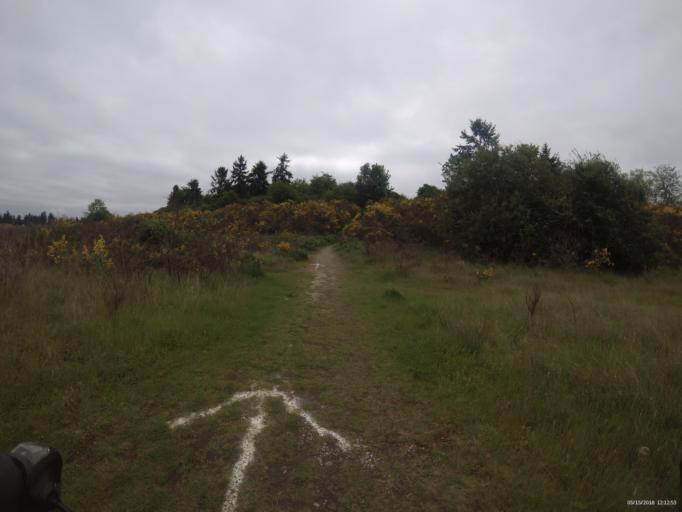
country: US
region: Washington
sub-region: Pierce County
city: Steilacoom
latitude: 47.1762
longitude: -122.5735
